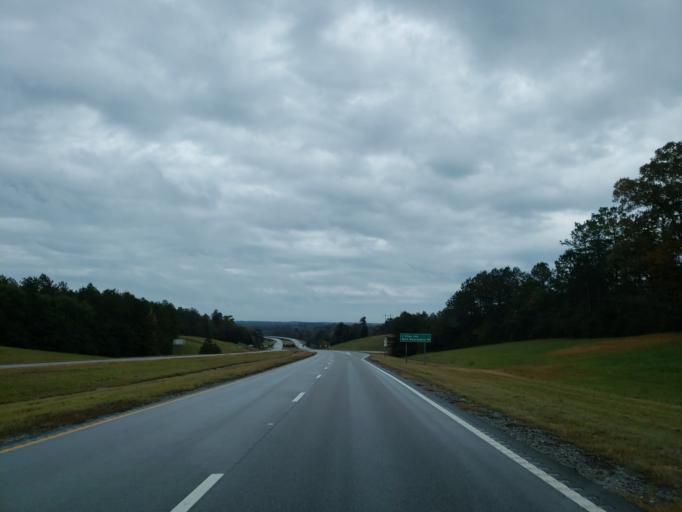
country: US
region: Mississippi
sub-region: Wayne County
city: Waynesboro
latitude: 31.6826
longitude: -88.6905
